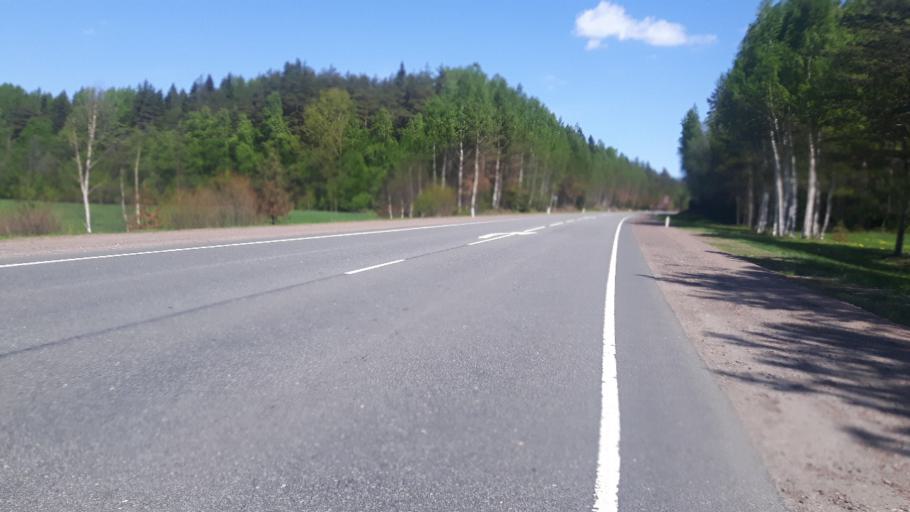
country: RU
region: Leningrad
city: Vysotsk
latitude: 60.6348
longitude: 28.2764
